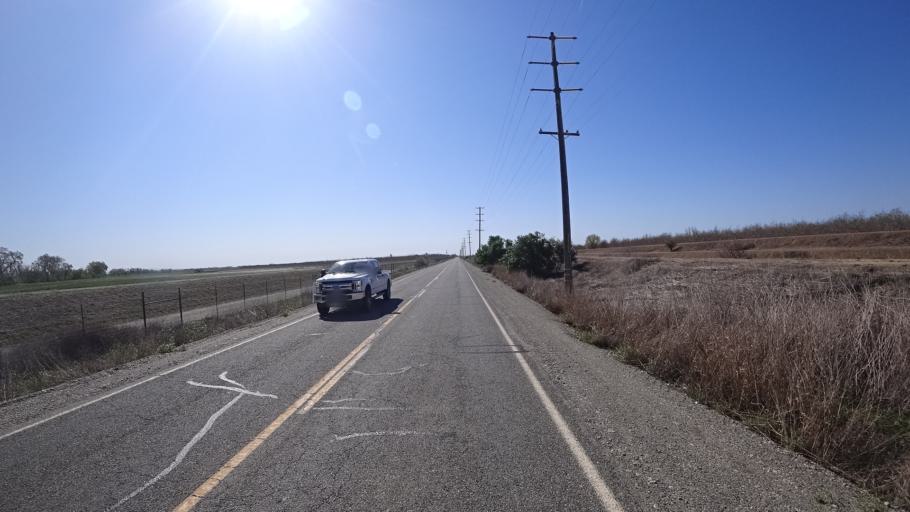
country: US
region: California
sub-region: Glenn County
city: Hamilton City
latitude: 39.7634
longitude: -122.0286
